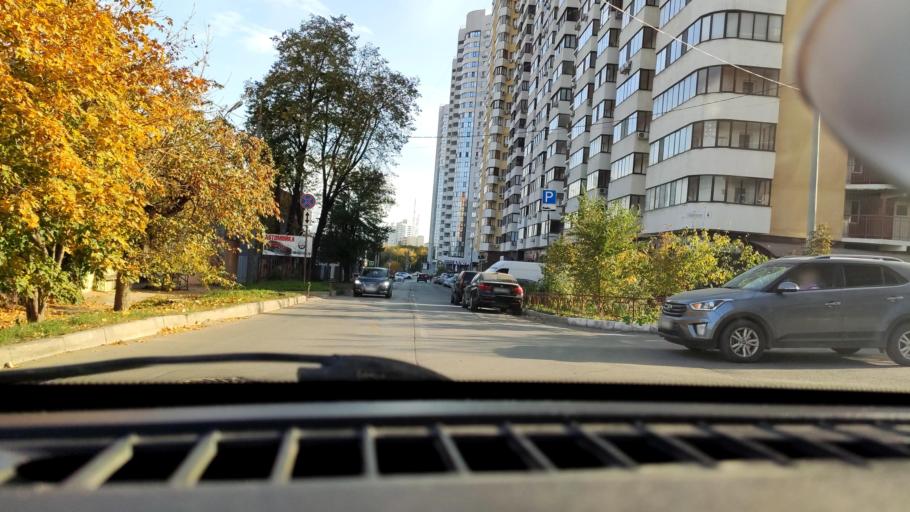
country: RU
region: Samara
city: Samara
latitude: 53.2172
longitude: 50.1629
